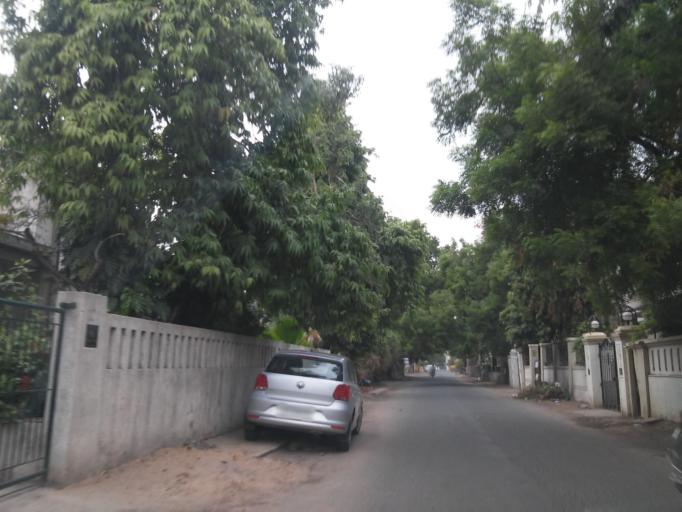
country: IN
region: Gujarat
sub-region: Ahmadabad
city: Ahmedabad
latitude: 23.0133
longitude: 72.5608
